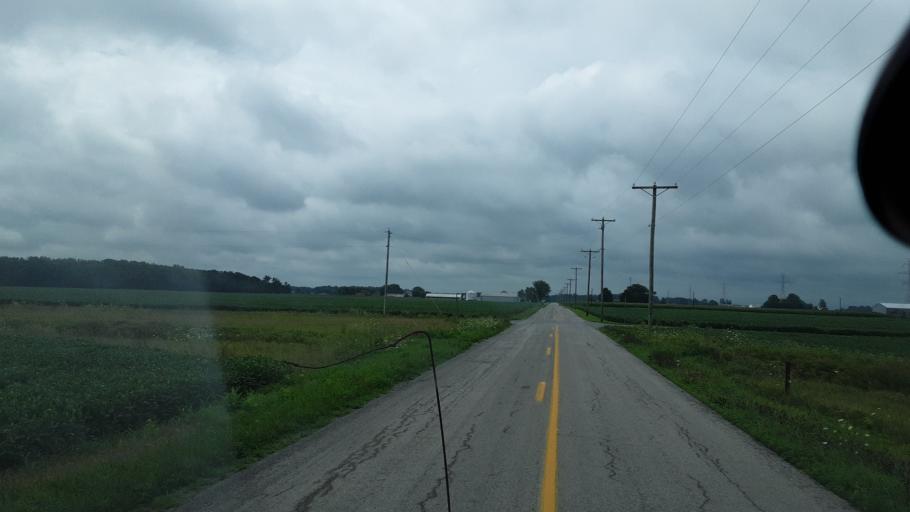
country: US
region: Indiana
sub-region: Allen County
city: Monroeville
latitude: 40.9640
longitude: -84.9690
